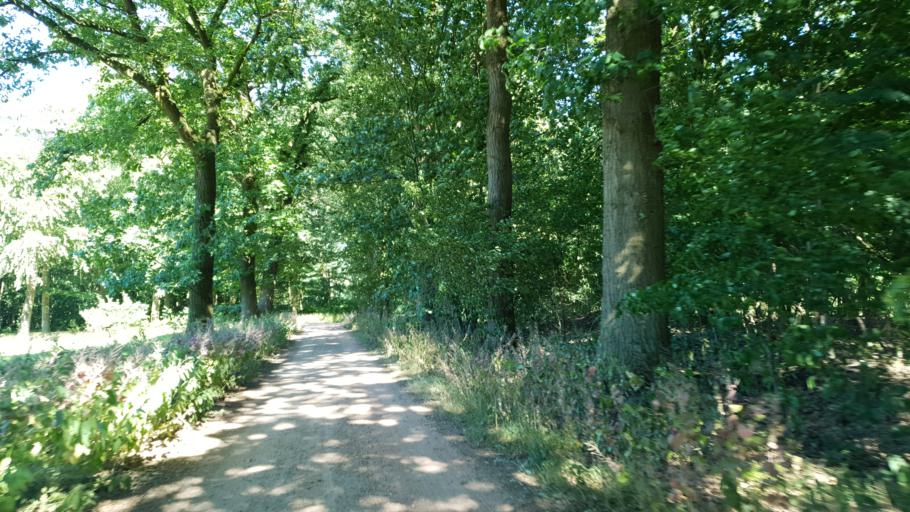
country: BE
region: Flanders
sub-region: Provincie Antwerpen
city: Merksplas
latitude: 51.3631
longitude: 4.8286
